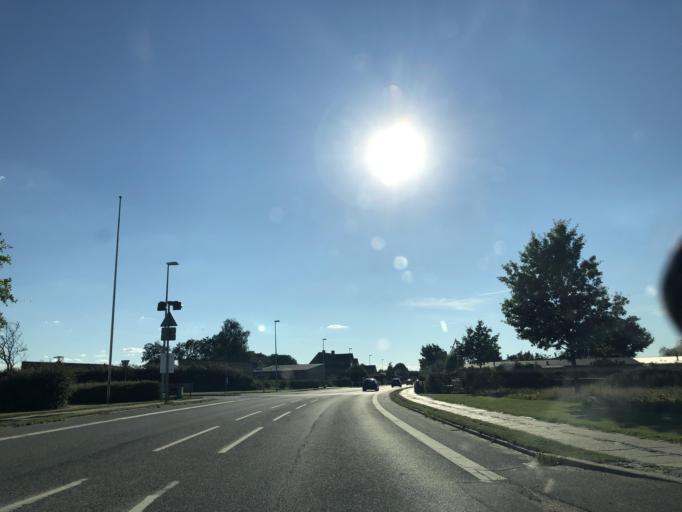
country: DK
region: North Denmark
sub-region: Mariagerfjord Kommune
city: Hobro
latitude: 56.6289
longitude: 9.8092
